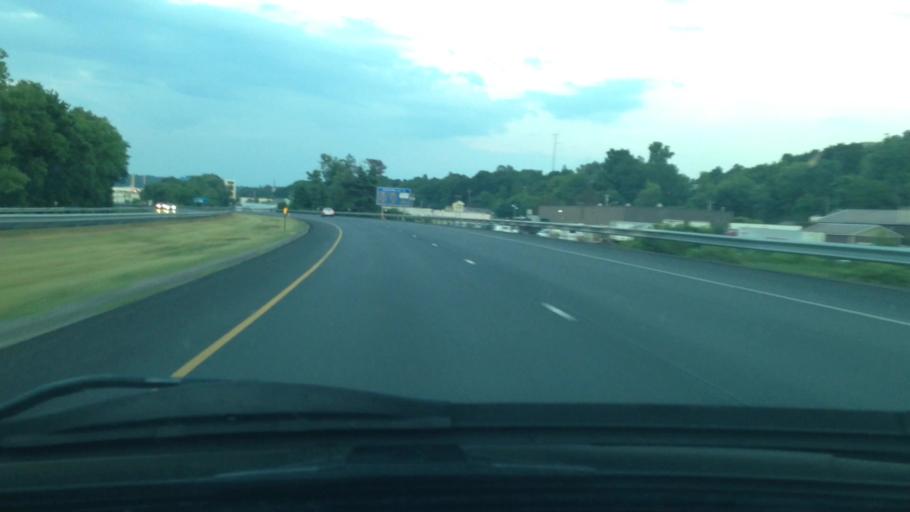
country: US
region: New York
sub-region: Montgomery County
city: Canajoharie
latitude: 42.9065
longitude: -74.5853
